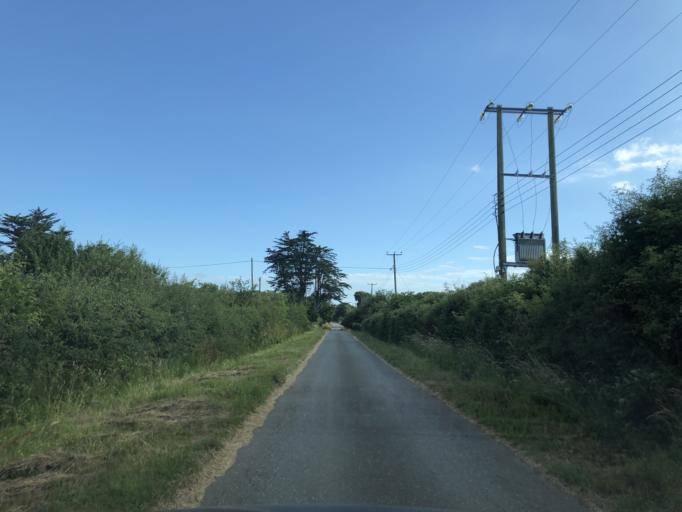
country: GB
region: England
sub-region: Isle of Wight
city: Shalfleet
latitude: 50.7078
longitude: -1.4494
